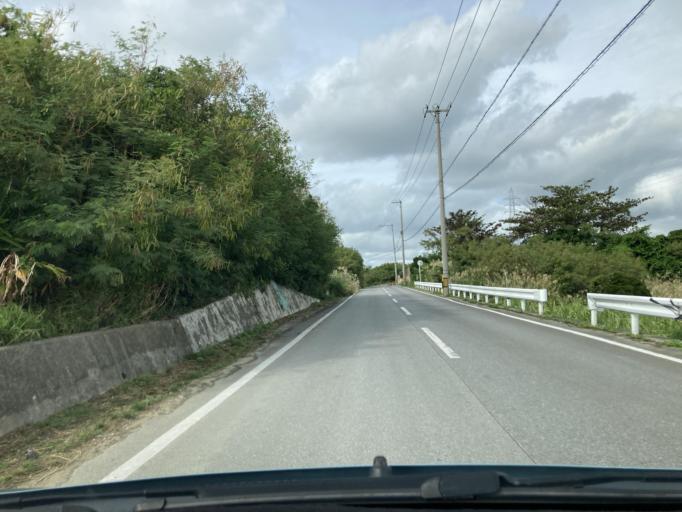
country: JP
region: Okinawa
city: Itoman
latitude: 26.1132
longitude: 127.6887
